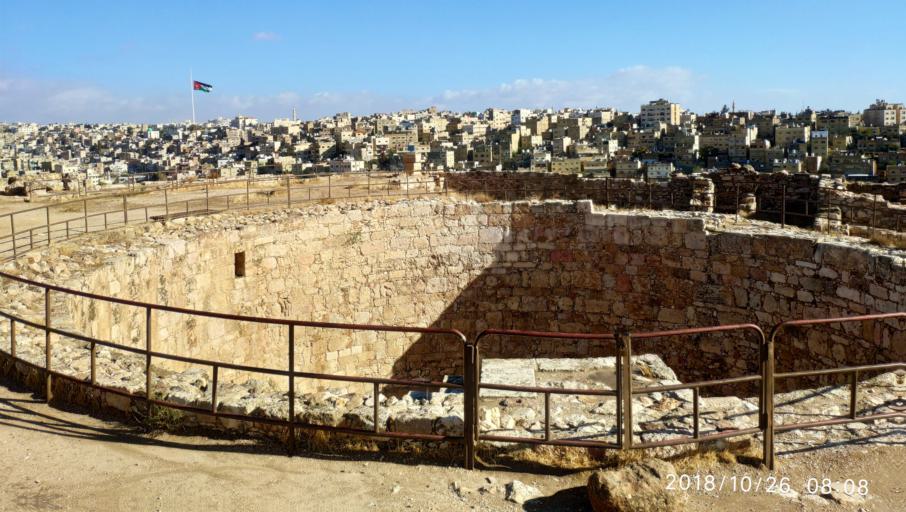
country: JO
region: Amman
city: Amman
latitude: 31.9554
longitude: 35.9346
